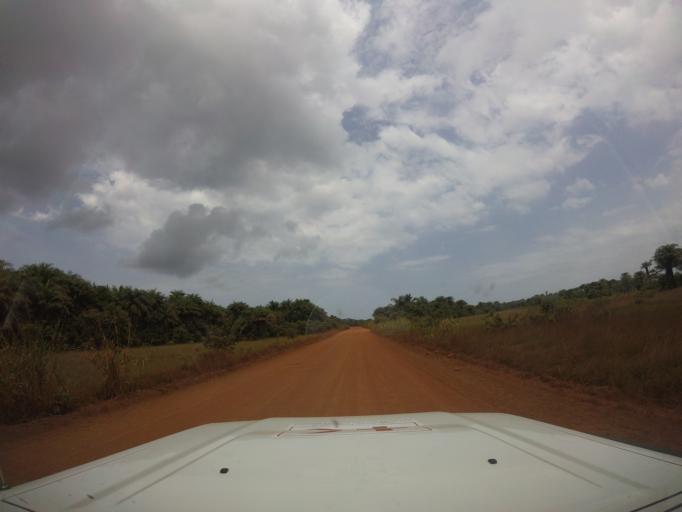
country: LR
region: Grand Cape Mount
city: Robertsport
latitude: 6.7484
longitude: -11.3437
